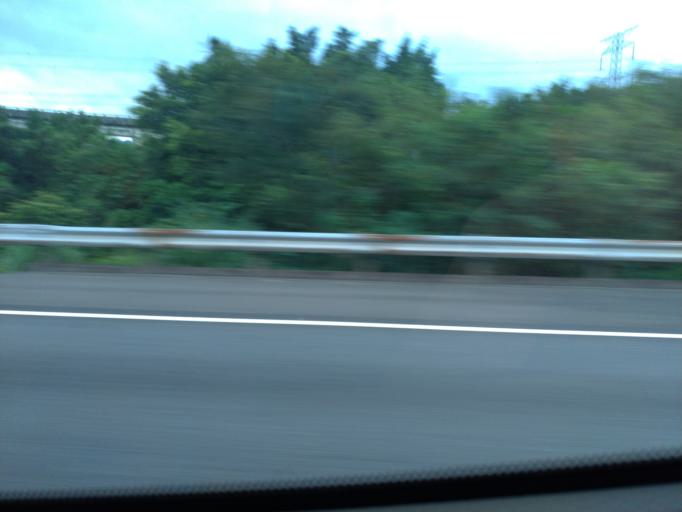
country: TW
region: Taiwan
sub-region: Taoyuan
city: Taoyuan
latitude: 24.9386
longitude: 121.3228
